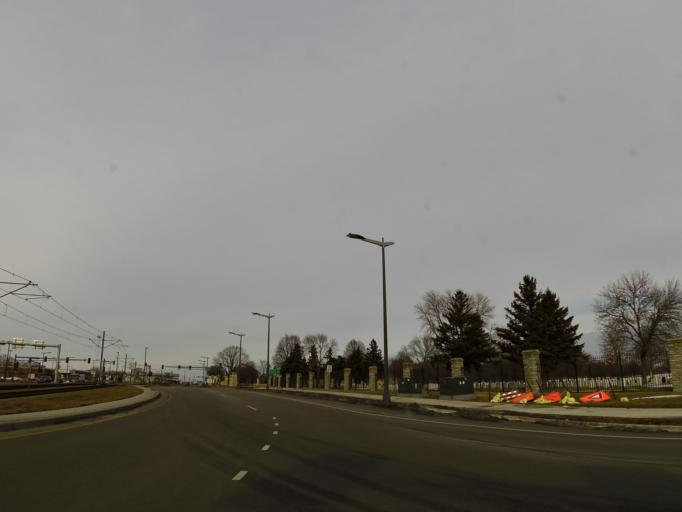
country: US
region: Minnesota
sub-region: Hennepin County
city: Richfield
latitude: 44.8632
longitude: -93.2229
